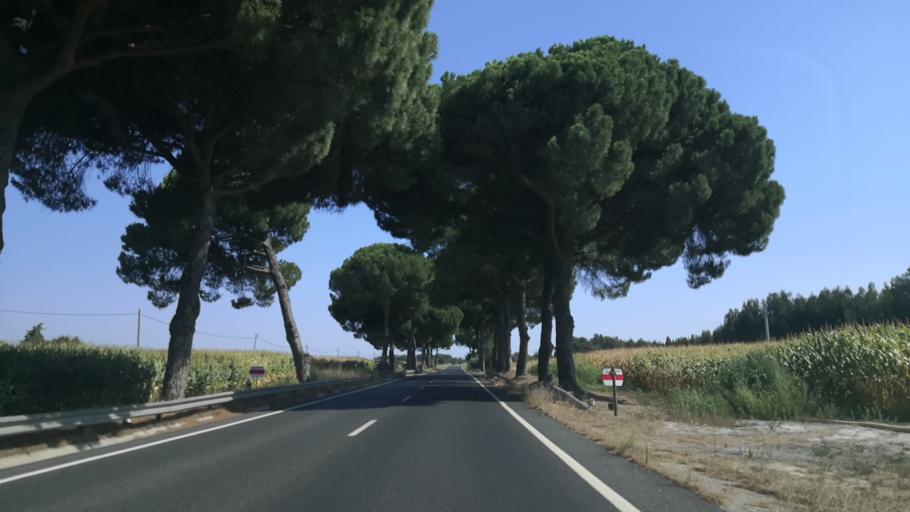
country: PT
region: Santarem
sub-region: Benavente
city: Poceirao
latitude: 38.7300
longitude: -8.6473
